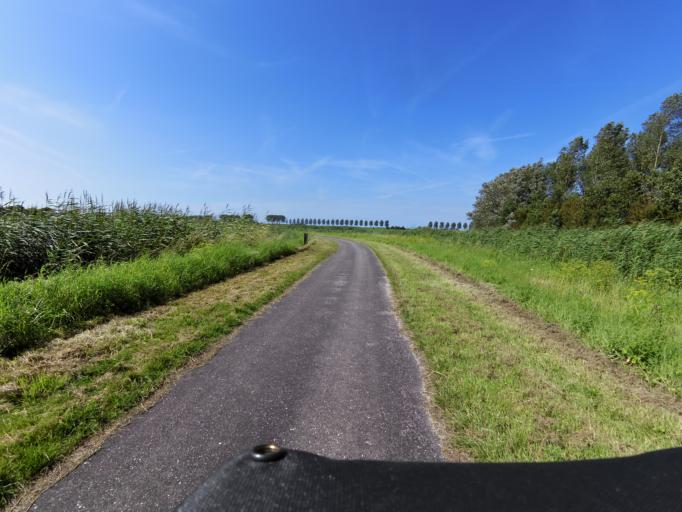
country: NL
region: South Holland
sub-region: Gemeente Goeree-Overflakkee
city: Dirksland
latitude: 51.7139
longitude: 4.1355
